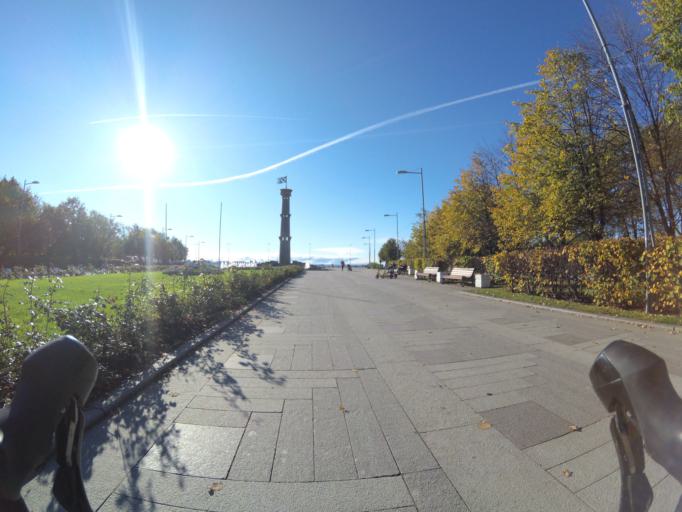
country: RU
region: Leningrad
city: Untolovo
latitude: 59.9825
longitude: 30.2011
